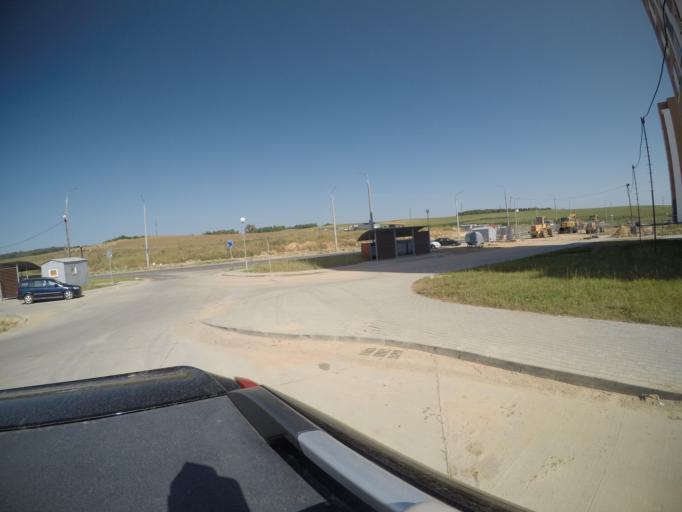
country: BY
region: Grodnenskaya
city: Hrodna
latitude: 53.7223
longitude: 23.8817
